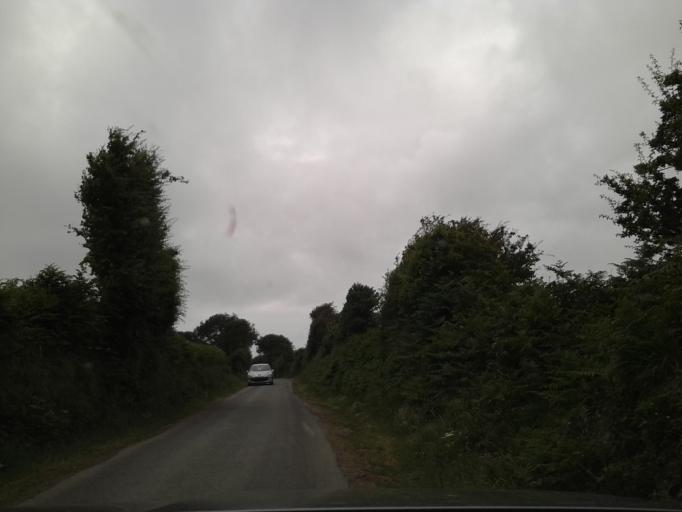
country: FR
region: Lower Normandy
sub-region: Departement de la Manche
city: Beaumont-Hague
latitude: 49.6870
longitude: -1.8760
